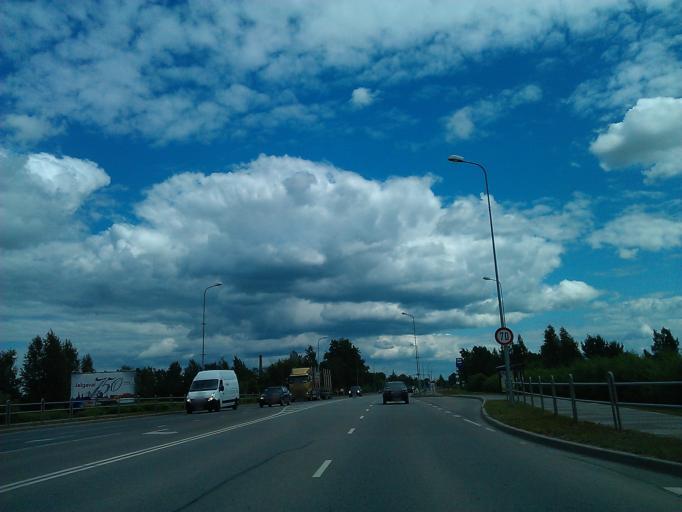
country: LV
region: Jelgava
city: Jelgava
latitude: 56.6533
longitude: 23.6691
